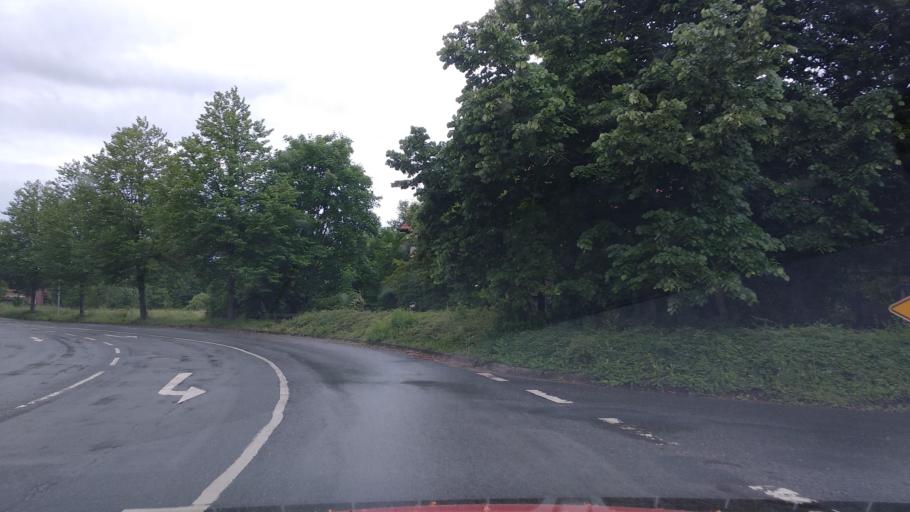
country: DE
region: Lower Saxony
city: Auhagen
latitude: 52.3984
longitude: 9.2894
